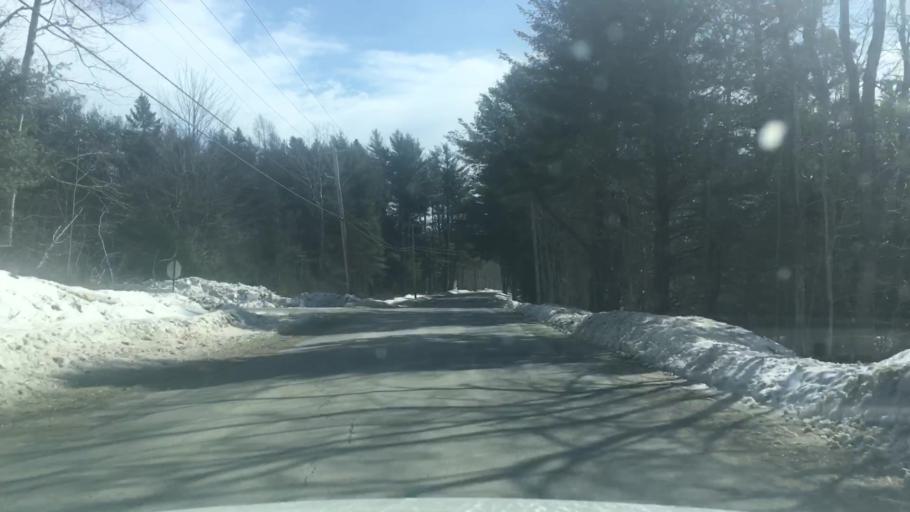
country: US
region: Maine
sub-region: Penobscot County
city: Holden
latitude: 44.7538
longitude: -68.6349
